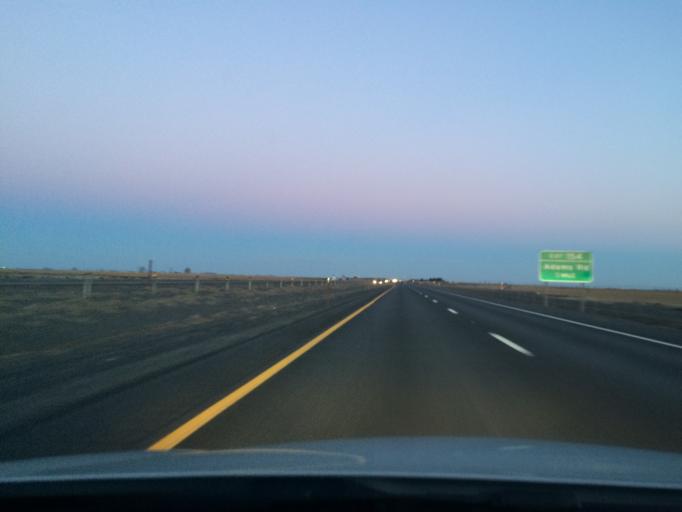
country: US
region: Washington
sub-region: Grant County
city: Quincy
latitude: 47.1034
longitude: -119.7902
